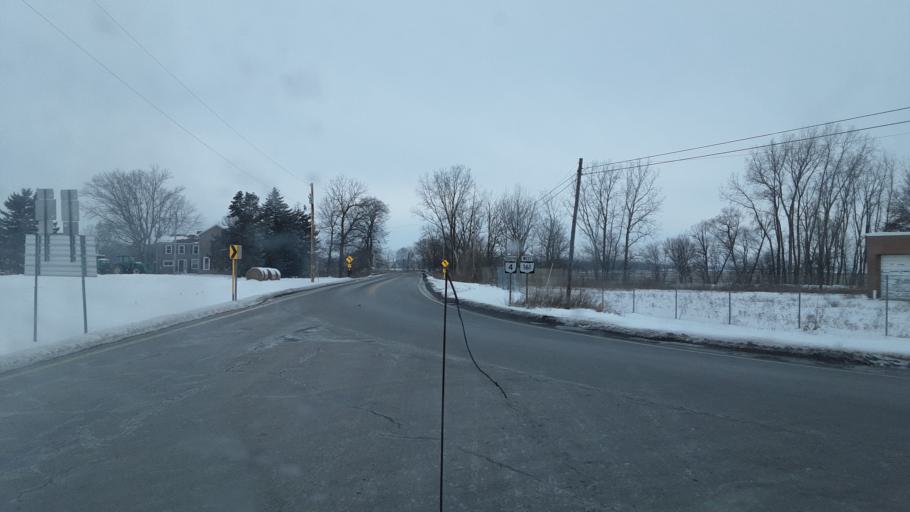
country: US
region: Ohio
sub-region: Champaign County
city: Mechanicsburg
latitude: 40.1238
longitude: -83.4922
